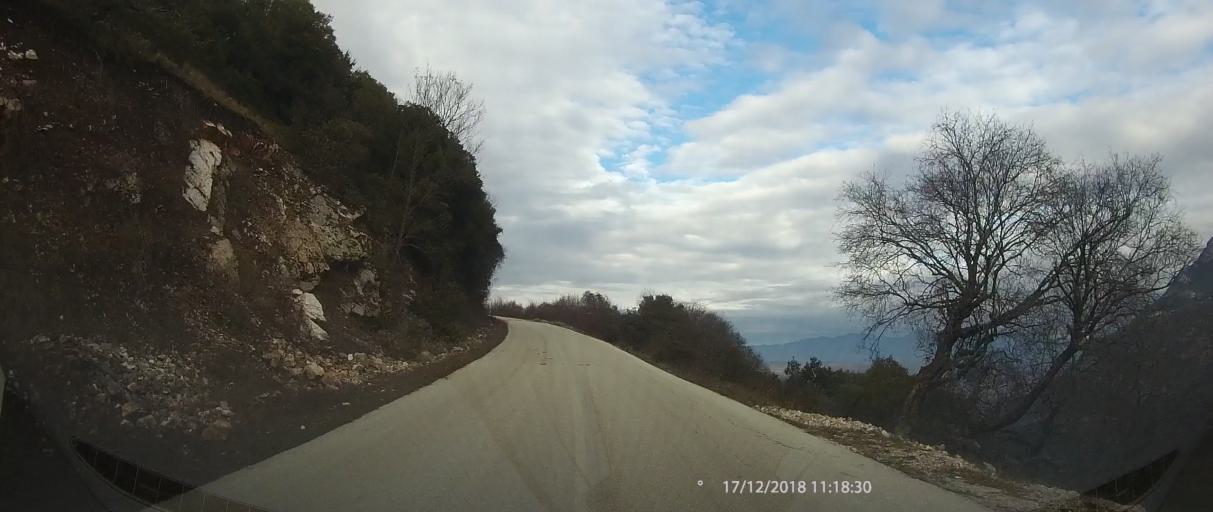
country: GR
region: Epirus
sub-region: Nomos Ioanninon
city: Kalpaki
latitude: 39.9542
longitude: 20.6579
